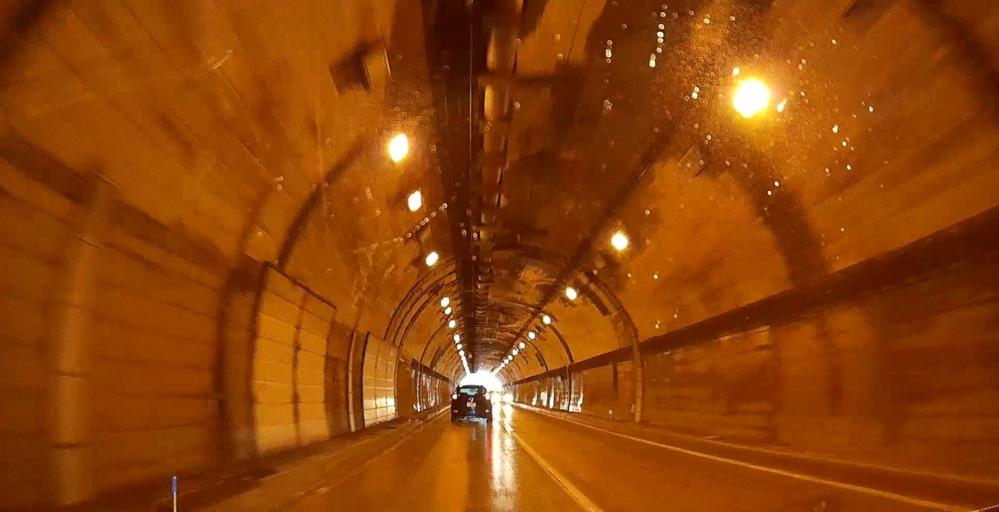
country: JP
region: Yamagata
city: Nagai
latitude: 38.0160
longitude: 139.8971
